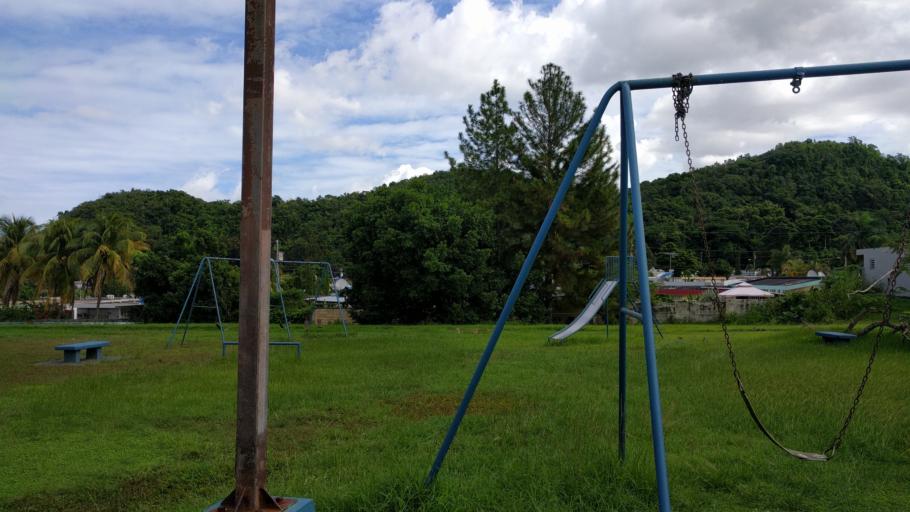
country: PR
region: Toa Baja
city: Candelaria Arenas
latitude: 18.4095
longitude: -66.2215
